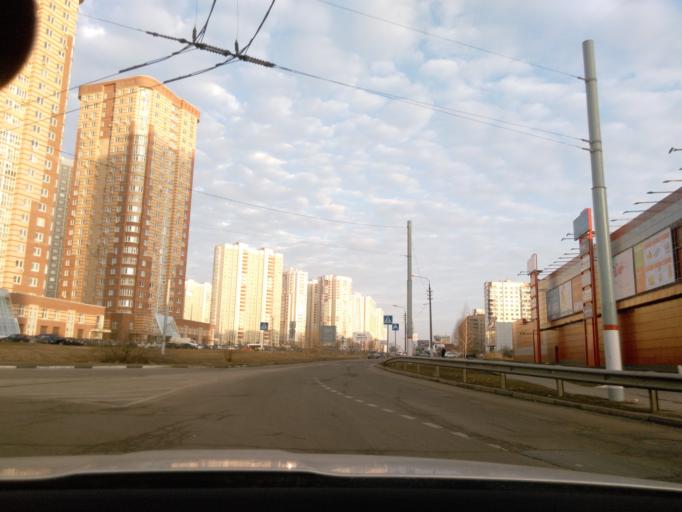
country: RU
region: Moscow
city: Khimki
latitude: 55.8988
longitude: 37.4089
